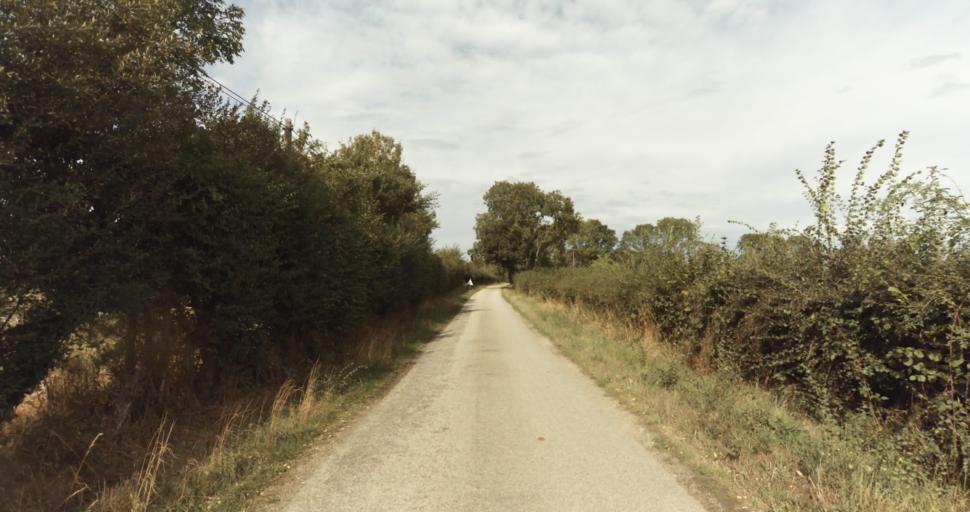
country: FR
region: Lower Normandy
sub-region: Departement du Calvados
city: La Vespiere
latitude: 48.9213
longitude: 0.3354
